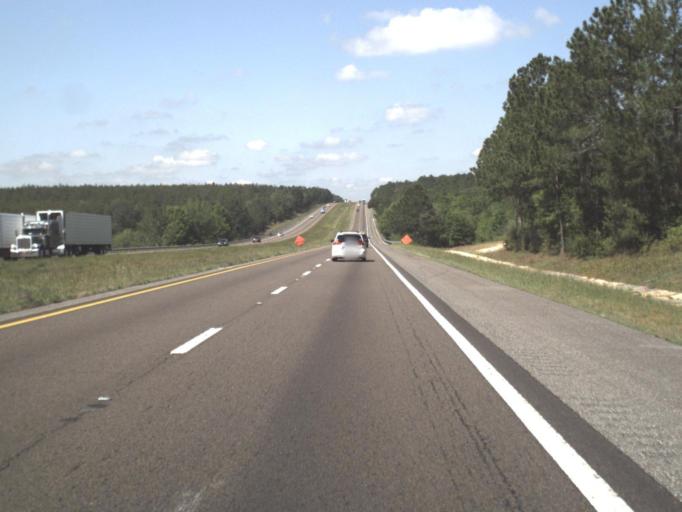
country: US
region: Florida
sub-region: Santa Rosa County
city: East Milton
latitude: 30.6820
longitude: -86.8044
